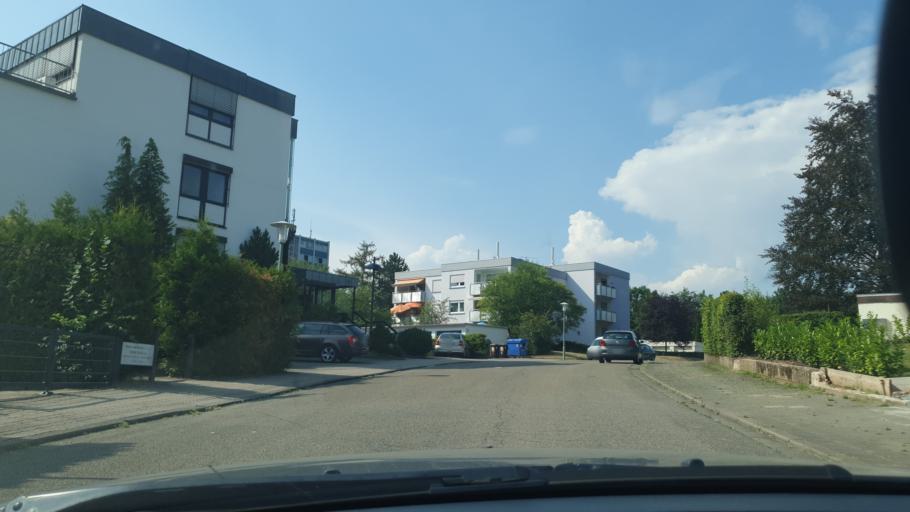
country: DE
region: Rheinland-Pfalz
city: Stelzenberg
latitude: 49.4291
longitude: 7.7272
